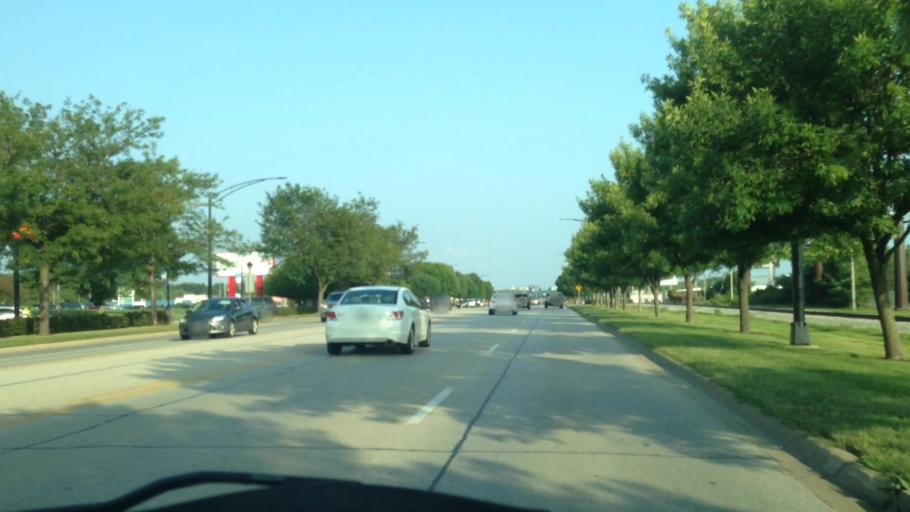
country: US
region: Iowa
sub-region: Johnson County
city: Coralville
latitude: 41.6835
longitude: -91.5995
